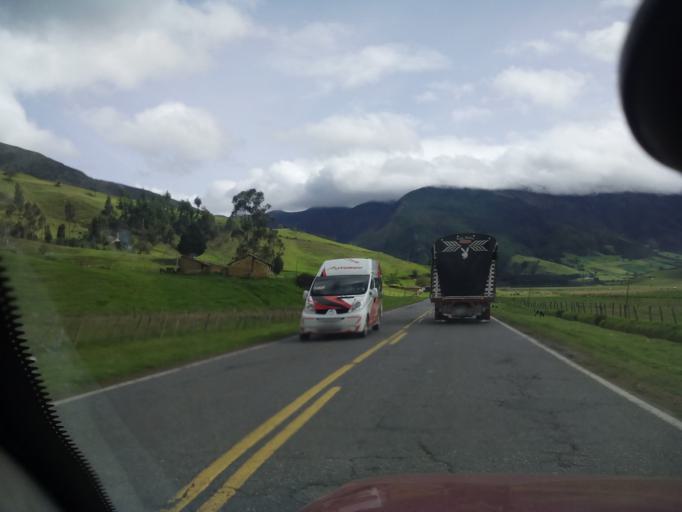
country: CO
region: Boyaca
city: Combita
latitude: 5.6956
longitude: -73.3682
